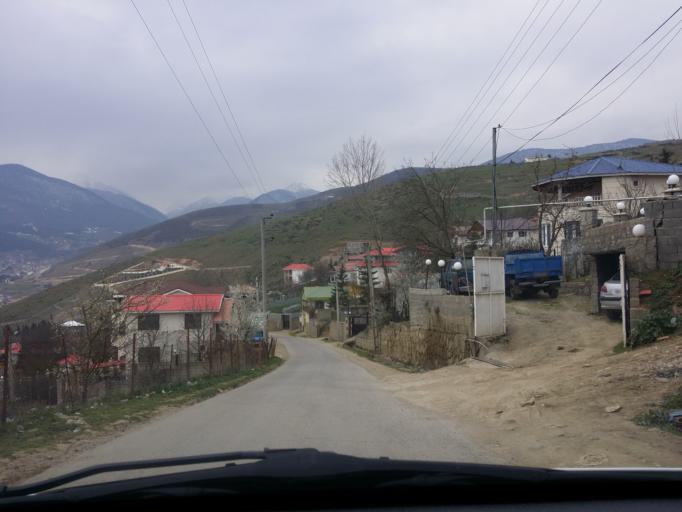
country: IR
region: Mazandaran
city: `Abbasabad
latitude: 36.5319
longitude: 51.1608
